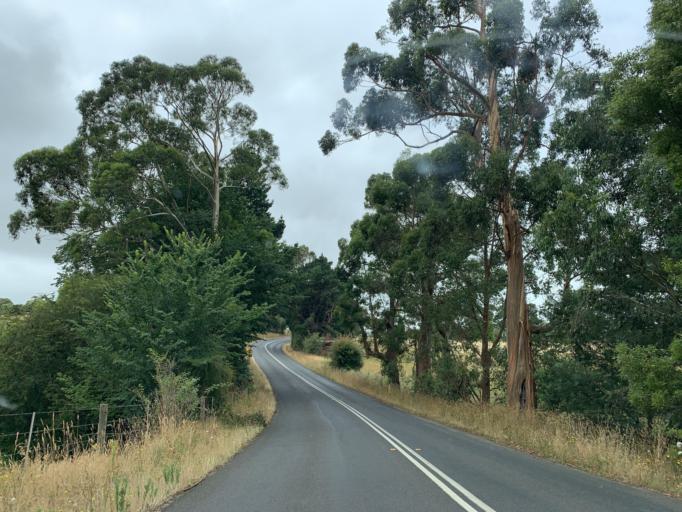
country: AU
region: Victoria
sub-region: Baw Baw
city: Warragul
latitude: -38.2394
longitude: 145.9326
